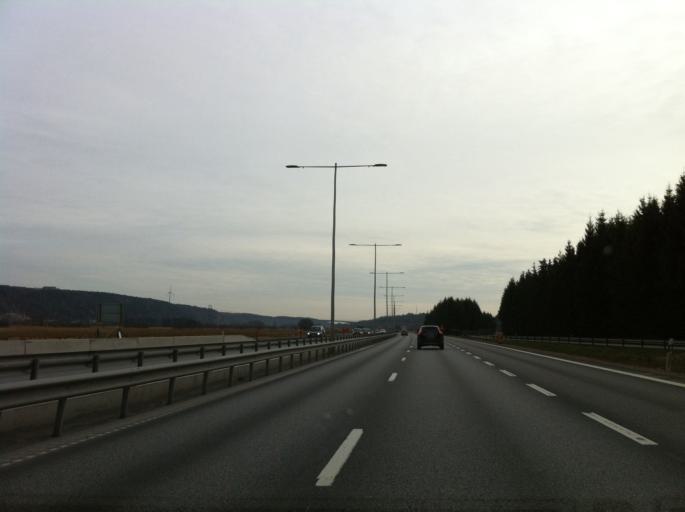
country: SE
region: Vaestra Goetaland
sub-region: Kungalvs Kommun
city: Kungalv
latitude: 57.8795
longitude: 11.9551
